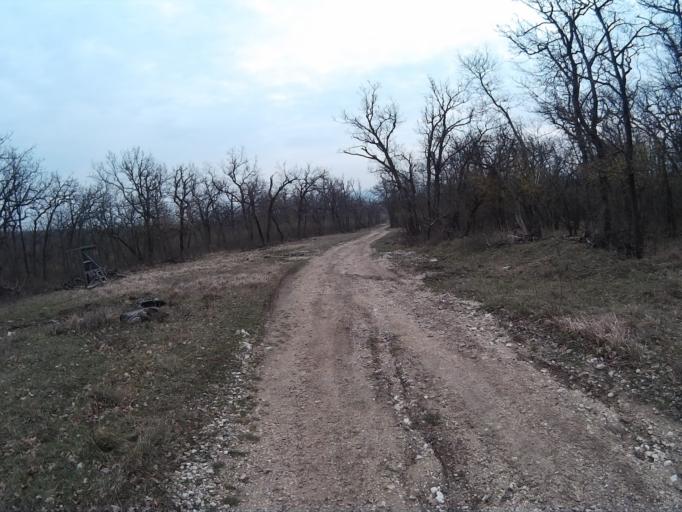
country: HU
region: Veszprem
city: Veszprem
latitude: 47.1685
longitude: 17.8675
